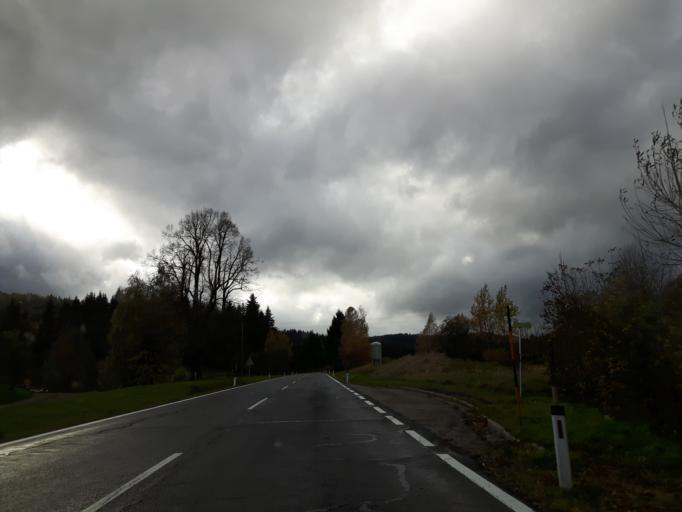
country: AT
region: Styria
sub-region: Politischer Bezirk Deutschlandsberg
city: Sankt Oswald ob Eibiswald
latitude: 46.7019
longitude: 15.1289
